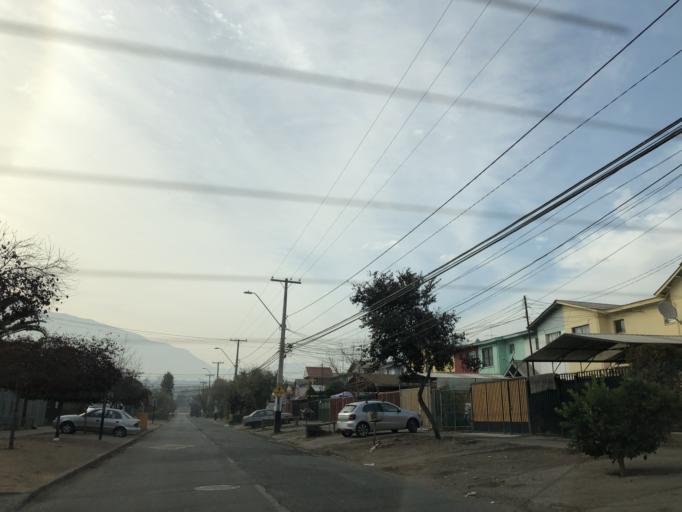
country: CL
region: Santiago Metropolitan
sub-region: Provincia de Cordillera
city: Puente Alto
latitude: -33.5841
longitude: -70.5538
